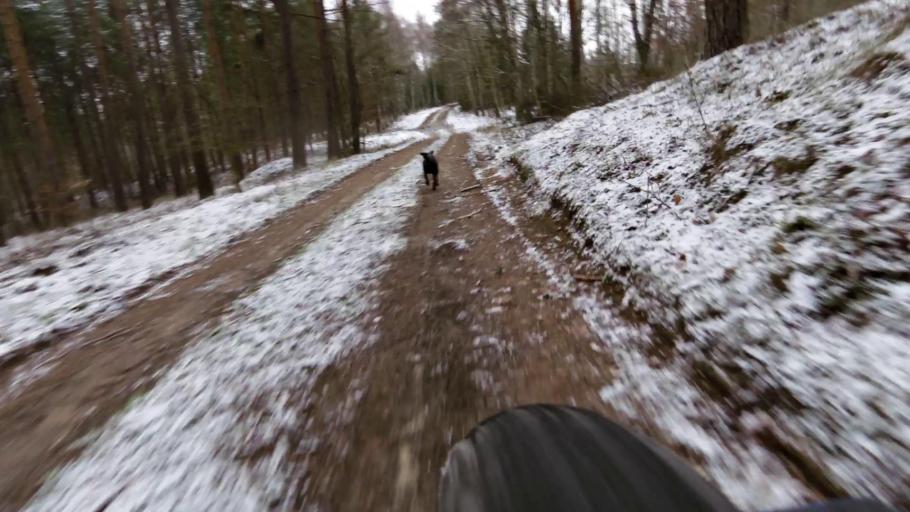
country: PL
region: West Pomeranian Voivodeship
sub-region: Powiat walecki
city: Miroslawiec
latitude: 53.3316
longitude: 16.1021
